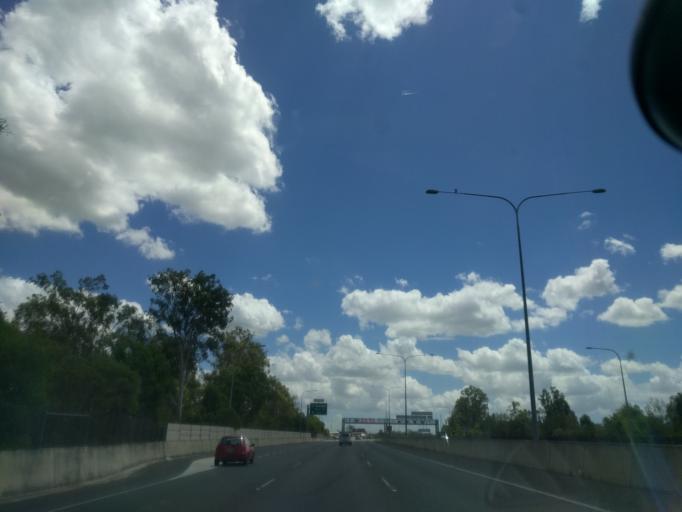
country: AU
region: Queensland
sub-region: Brisbane
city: Wacol
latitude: -27.5972
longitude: 152.9215
